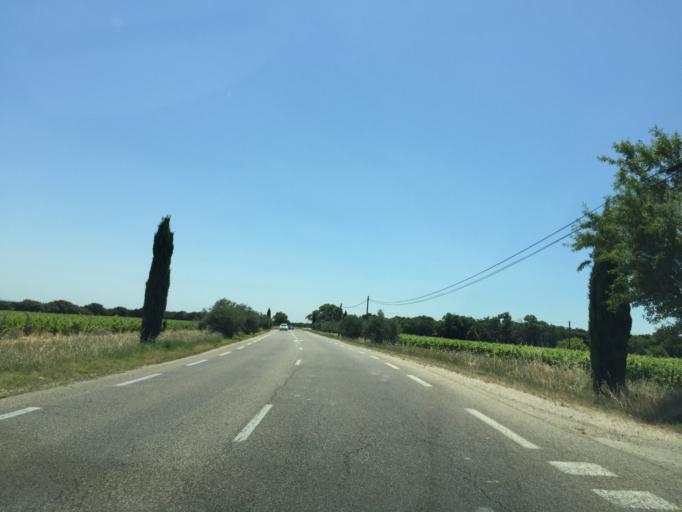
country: FR
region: Provence-Alpes-Cote d'Azur
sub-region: Departement du Vaucluse
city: Serignan-du-Comtat
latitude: 44.2100
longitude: 4.8684
